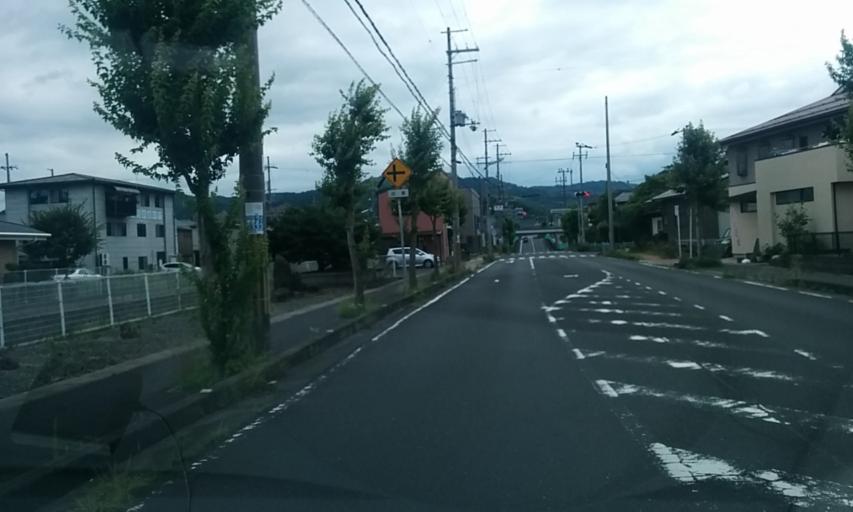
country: JP
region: Kyoto
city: Ayabe
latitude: 35.3034
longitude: 135.2620
